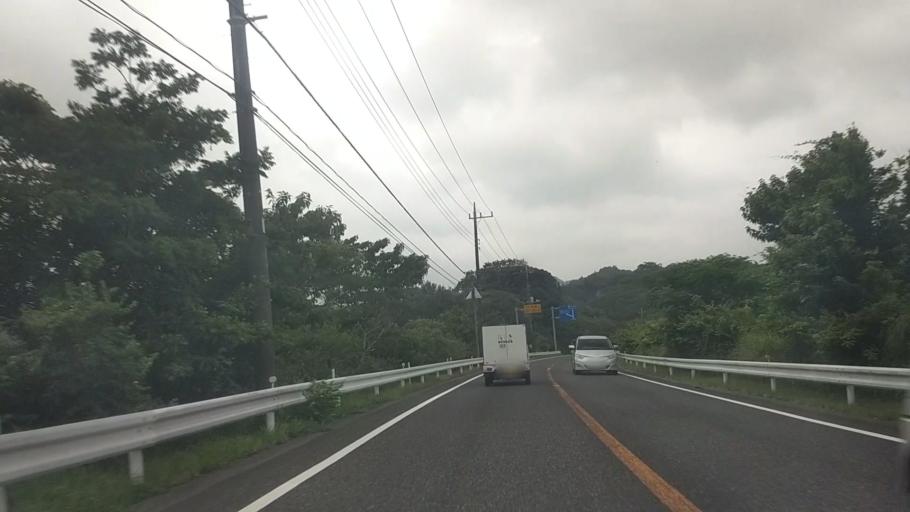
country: JP
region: Chiba
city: Kawaguchi
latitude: 35.1610
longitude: 140.0639
